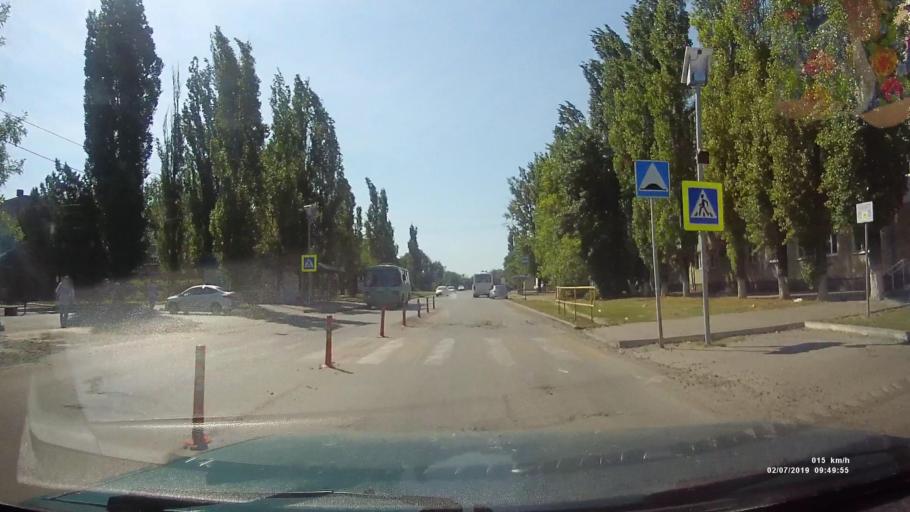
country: RU
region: Rostov
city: Azov
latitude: 47.1032
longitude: 39.4026
